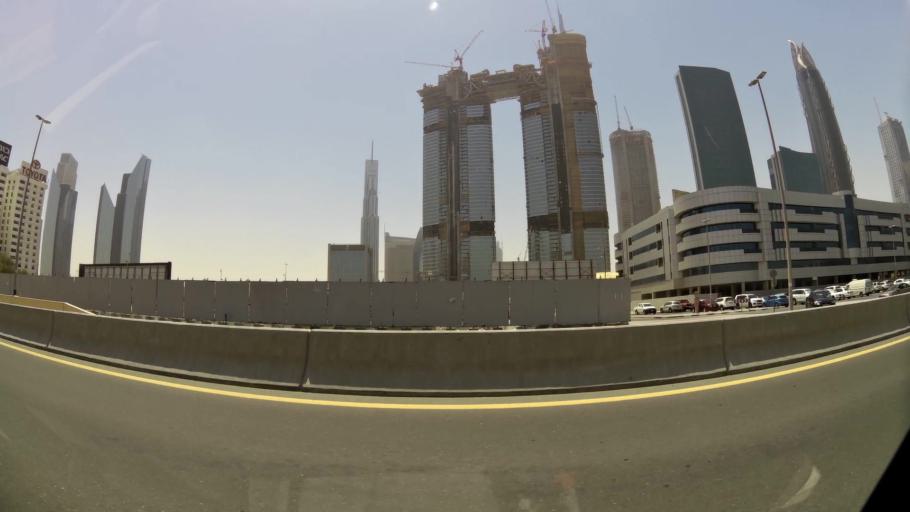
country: AE
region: Dubai
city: Dubai
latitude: 25.2038
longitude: 55.2674
